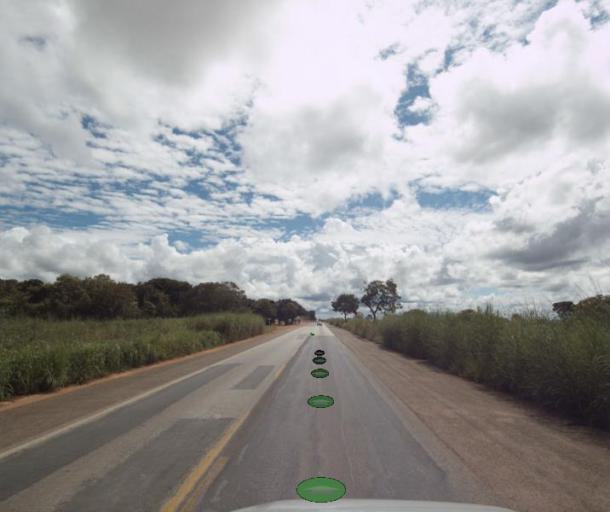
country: BR
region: Goias
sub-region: Uruacu
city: Uruacu
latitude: -14.3407
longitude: -49.1560
